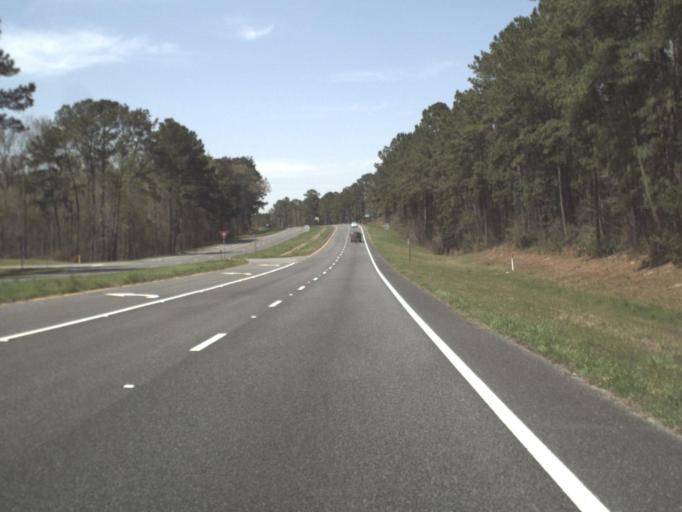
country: US
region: Florida
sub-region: Gadsden County
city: Midway
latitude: 30.5471
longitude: -84.4854
